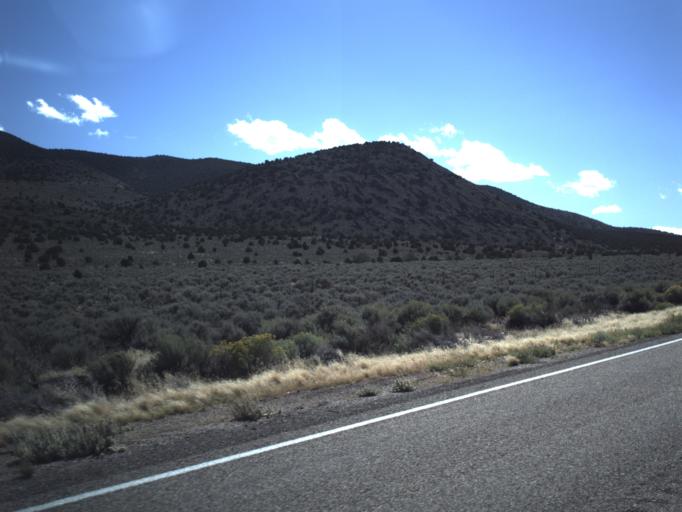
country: US
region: Utah
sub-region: Beaver County
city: Milford
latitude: 38.1473
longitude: -112.9598
